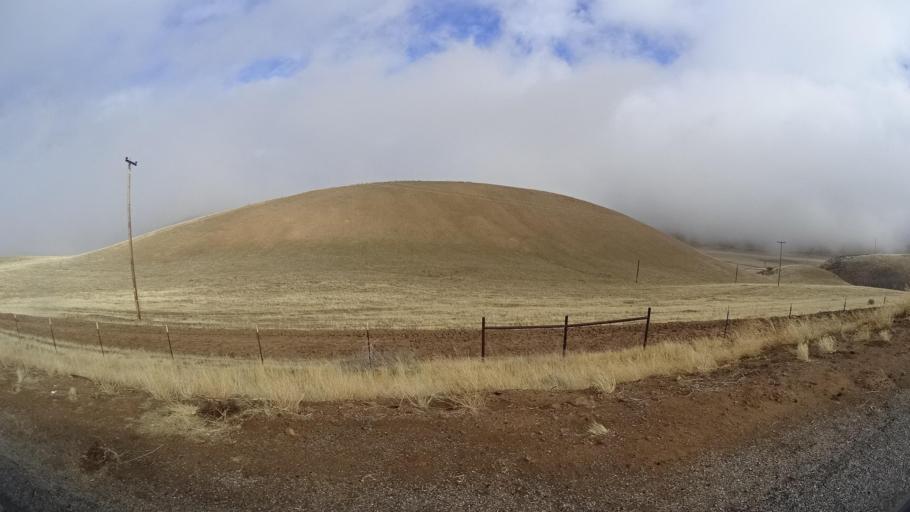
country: US
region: California
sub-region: Kern County
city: Maricopa
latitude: 34.9309
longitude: -119.4094
